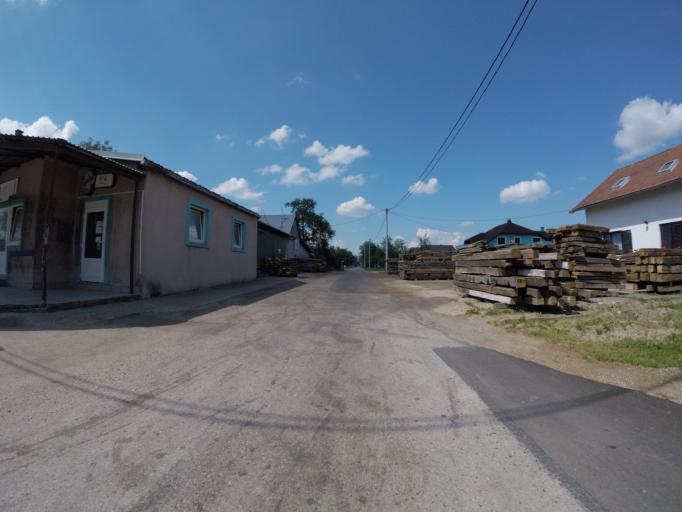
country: HR
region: Zagrebacka
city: Kuce
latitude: 45.6744
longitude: 16.1830
